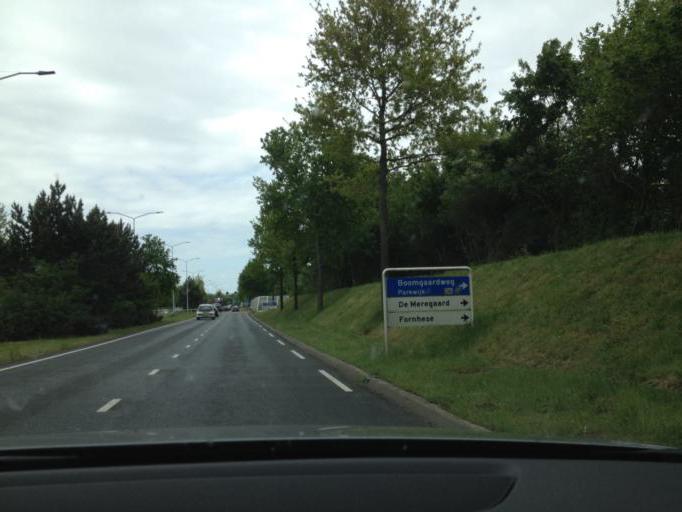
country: NL
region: Flevoland
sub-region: Gemeente Almere
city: Almere Stad
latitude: 52.3696
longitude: 5.2399
